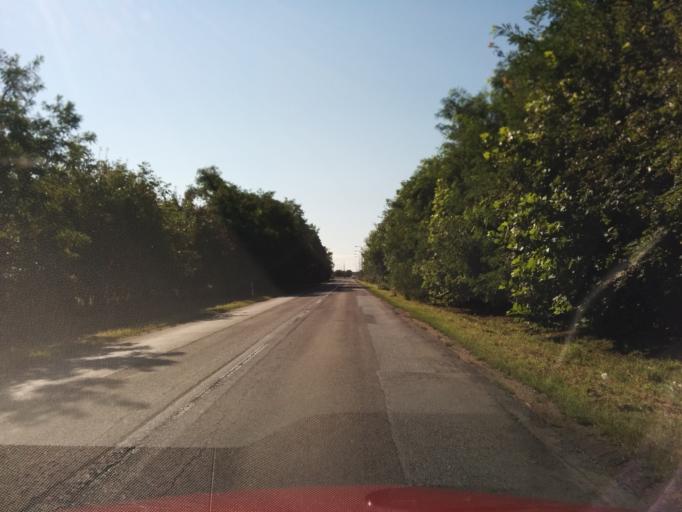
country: HU
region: Vas
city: Sarvar
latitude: 47.3630
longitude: 16.8948
